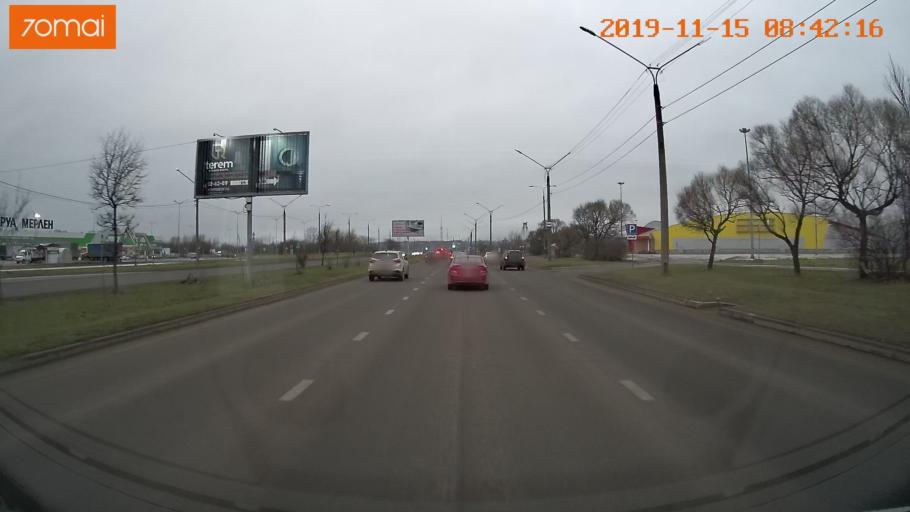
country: RU
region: Vologda
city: Cherepovets
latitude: 59.1017
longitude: 37.9089
